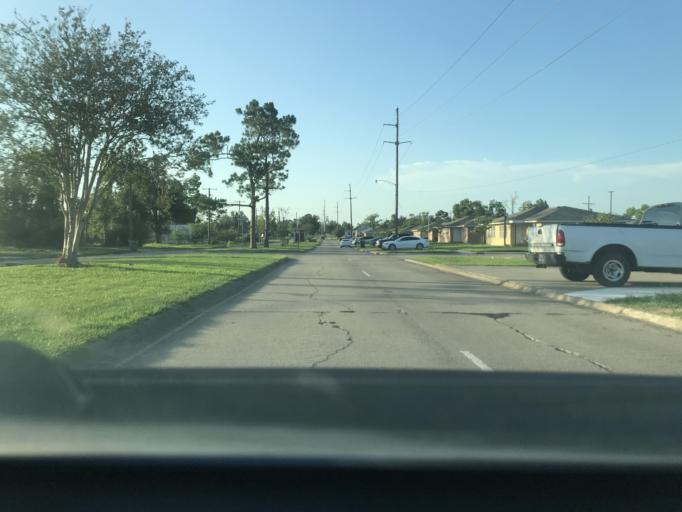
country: US
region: Louisiana
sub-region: Calcasieu Parish
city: Lake Charles
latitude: 30.2540
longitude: -93.1952
